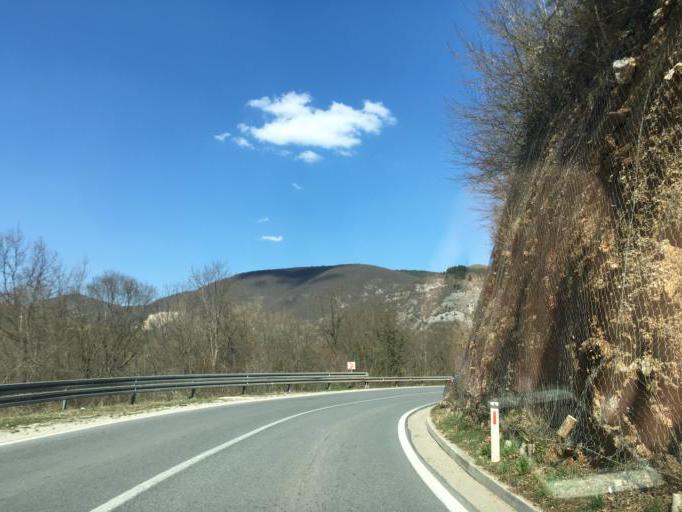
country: BA
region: Federation of Bosnia and Herzegovina
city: Divicani
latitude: 44.3647
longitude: 17.2960
